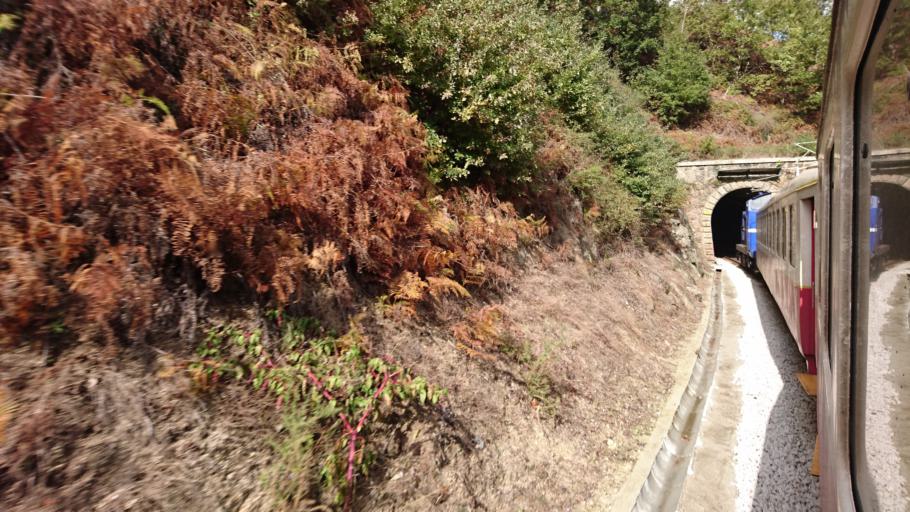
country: PT
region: Porto
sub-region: Marco de Canaveses
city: Marco de Canavezes
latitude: 41.1926
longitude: -8.1383
